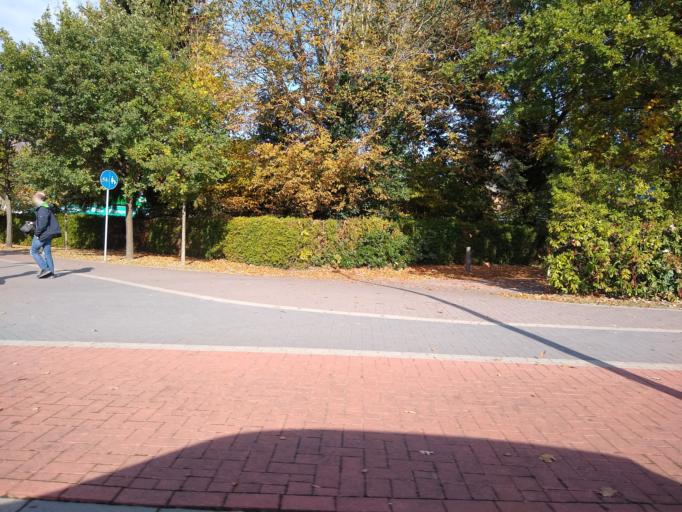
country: DE
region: Lower Saxony
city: Oldenburg
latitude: 53.1597
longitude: 8.1723
